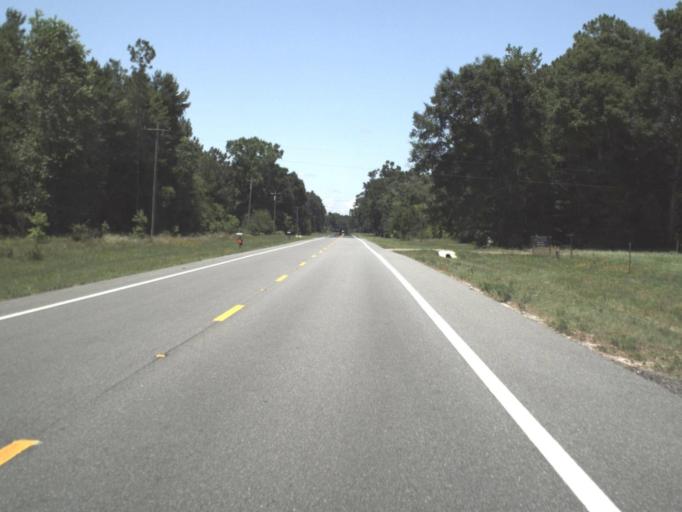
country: US
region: Florida
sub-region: Lafayette County
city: Mayo
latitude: 29.9402
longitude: -82.9487
